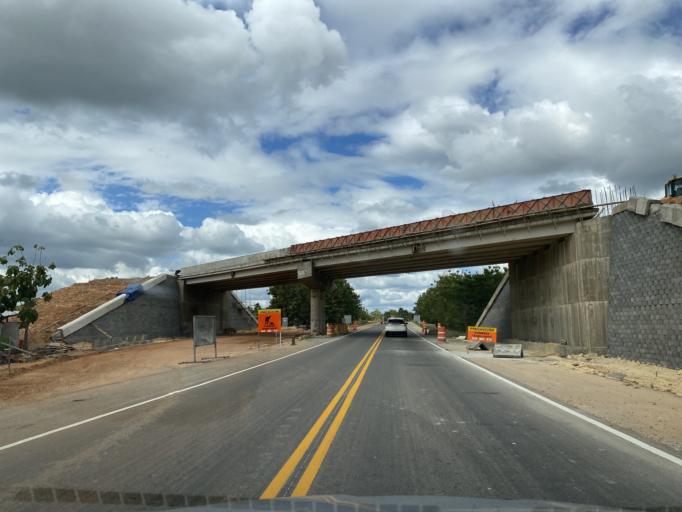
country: DO
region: Santo Domingo
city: Guerra
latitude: 18.5609
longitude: -69.7676
